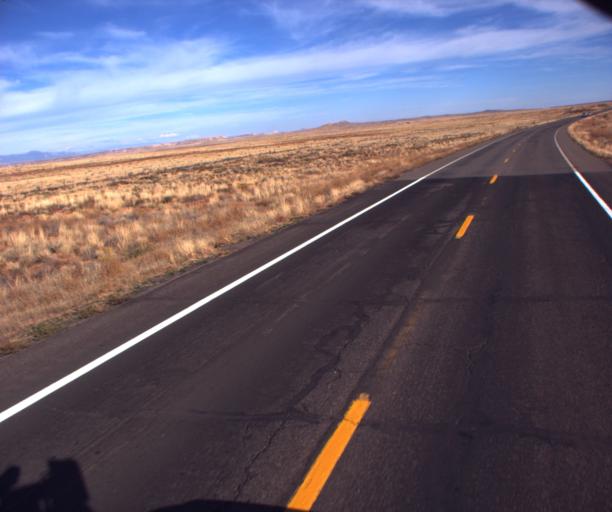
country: US
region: Arizona
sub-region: Apache County
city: Lukachukai
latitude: 36.9582
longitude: -109.3085
